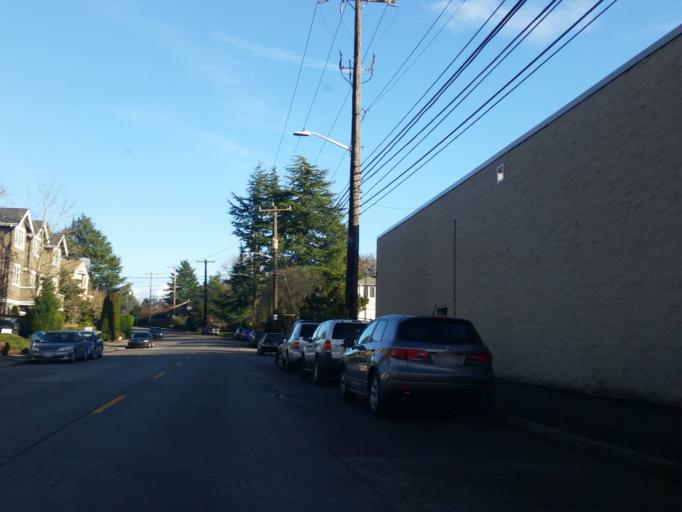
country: US
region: Washington
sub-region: King County
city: Yarrow Point
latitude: 47.6685
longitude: -122.2837
